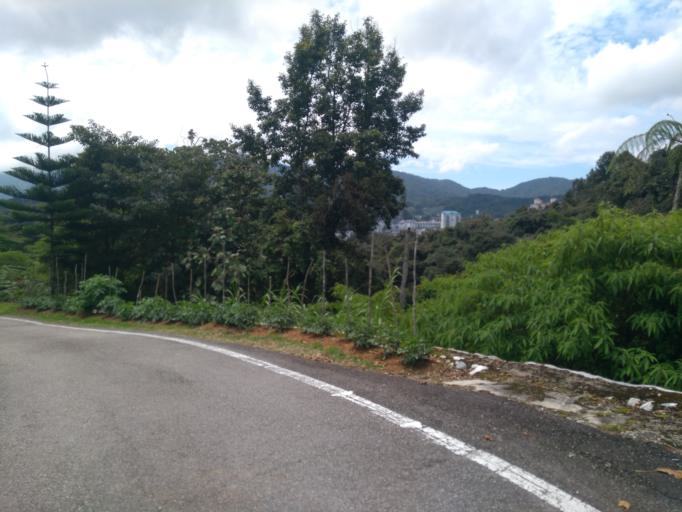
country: MY
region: Pahang
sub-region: Cameron Highlands
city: Tanah Rata
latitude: 4.4829
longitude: 101.3851
